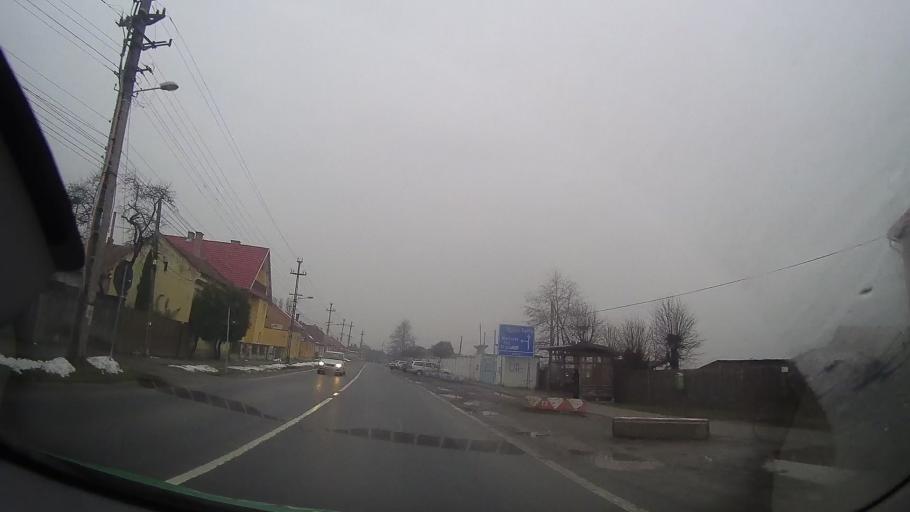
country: RO
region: Harghita
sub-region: Municipiul Gheorgheni
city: Gheorgheni
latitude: 46.7241
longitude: 25.5933
